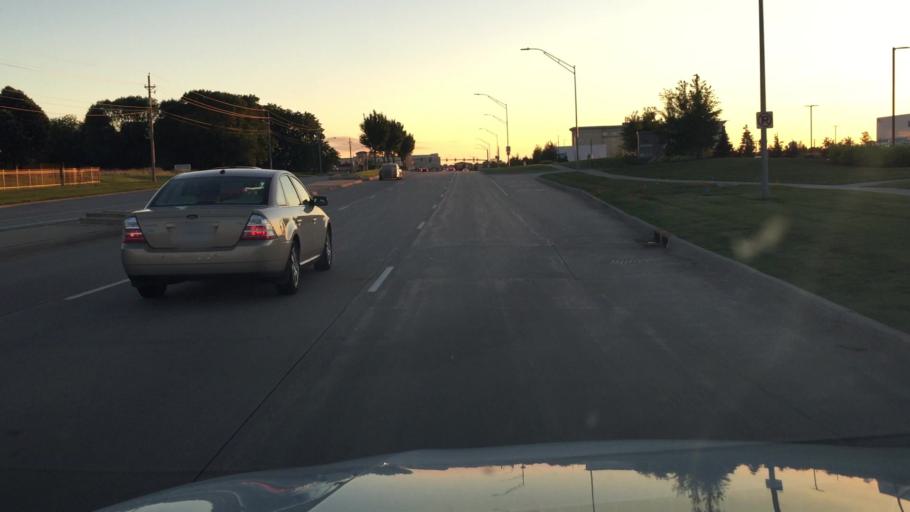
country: US
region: Iowa
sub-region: Polk County
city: Clive
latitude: 41.5592
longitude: -93.7861
